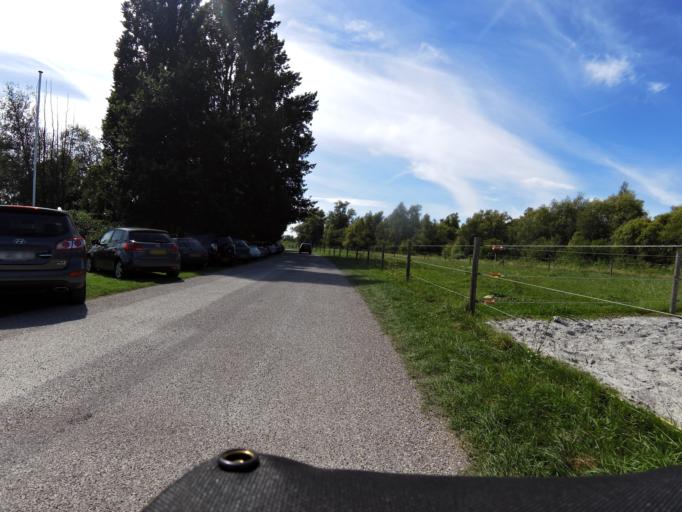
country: NL
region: South Holland
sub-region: Gemeente Sliedrecht
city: Sliedrecht
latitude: 51.7772
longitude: 4.7608
